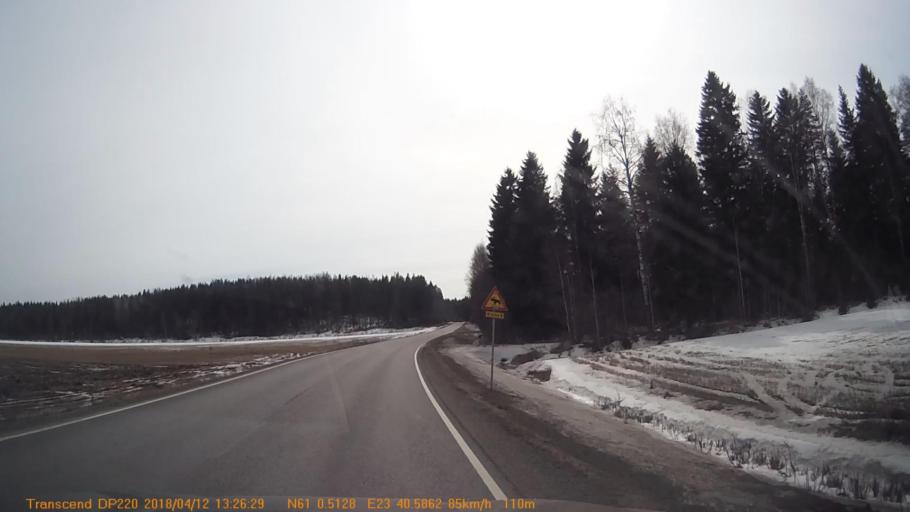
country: FI
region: Pirkanmaa
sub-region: Etelae-Pirkanmaa
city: Kylmaekoski
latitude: 61.0082
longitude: 23.6765
